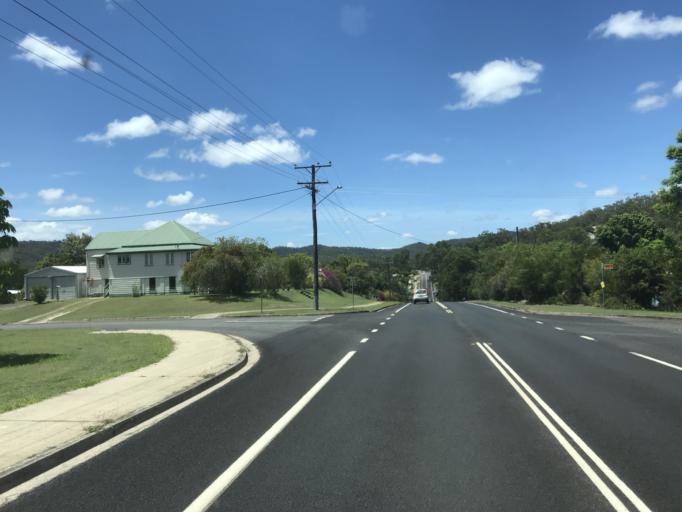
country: AU
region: Queensland
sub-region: Tablelands
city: Atherton
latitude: -17.3914
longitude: 145.3873
